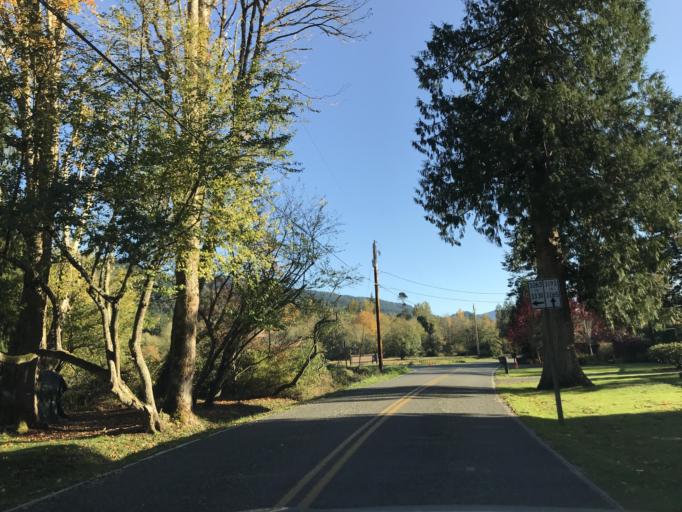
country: US
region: Washington
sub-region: Whatcom County
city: Sudden Valley
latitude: 48.7340
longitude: -122.3164
